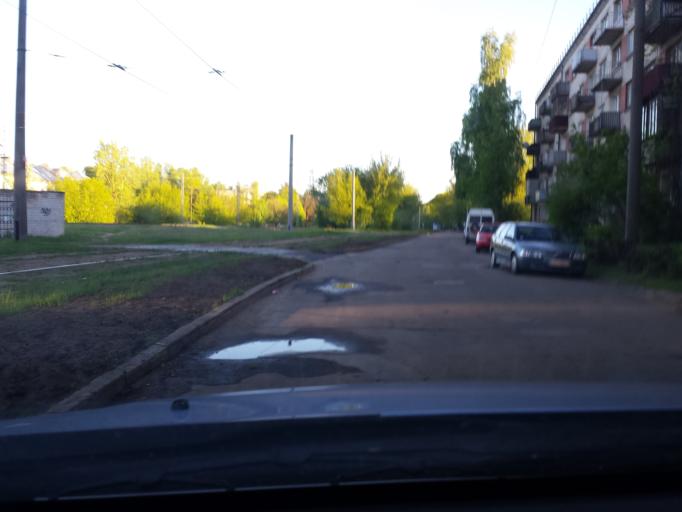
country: LV
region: Riga
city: Jaunciems
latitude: 57.0088
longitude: 24.1256
